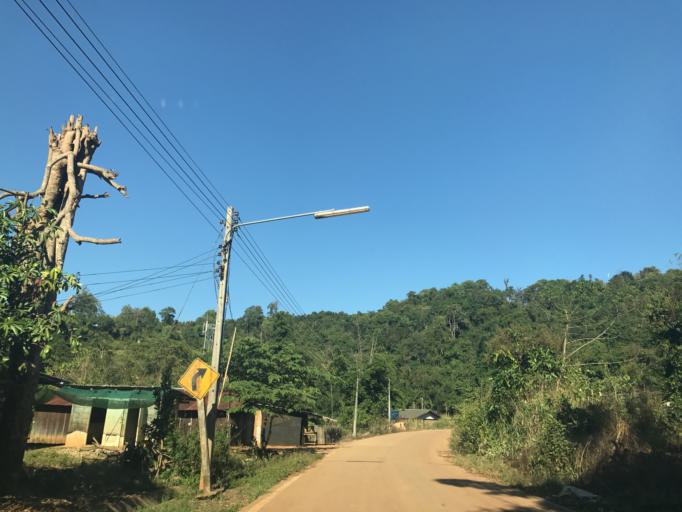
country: TH
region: Tak
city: Phop Phra
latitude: 16.5691
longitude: 98.8169
